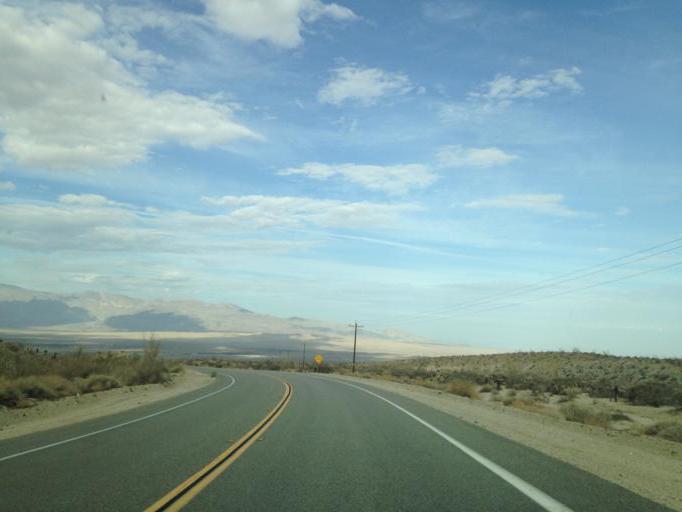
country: US
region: California
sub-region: San Diego County
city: Borrego Springs
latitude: 33.1608
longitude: -116.3382
